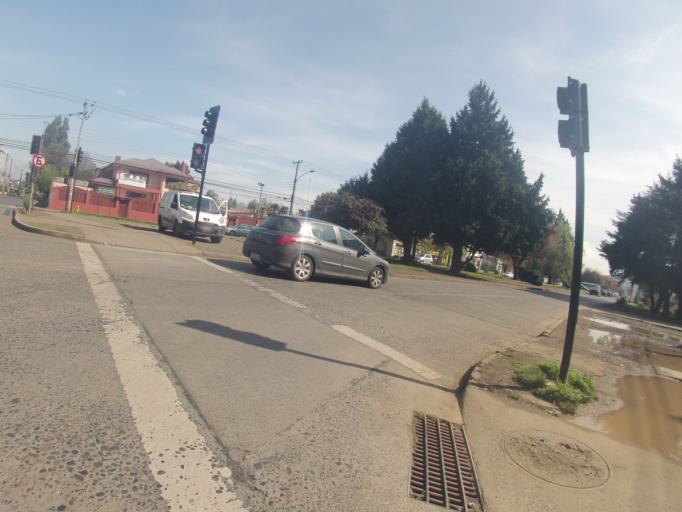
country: CL
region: Araucania
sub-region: Provincia de Cautin
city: Temuco
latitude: -38.7348
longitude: -72.6005
